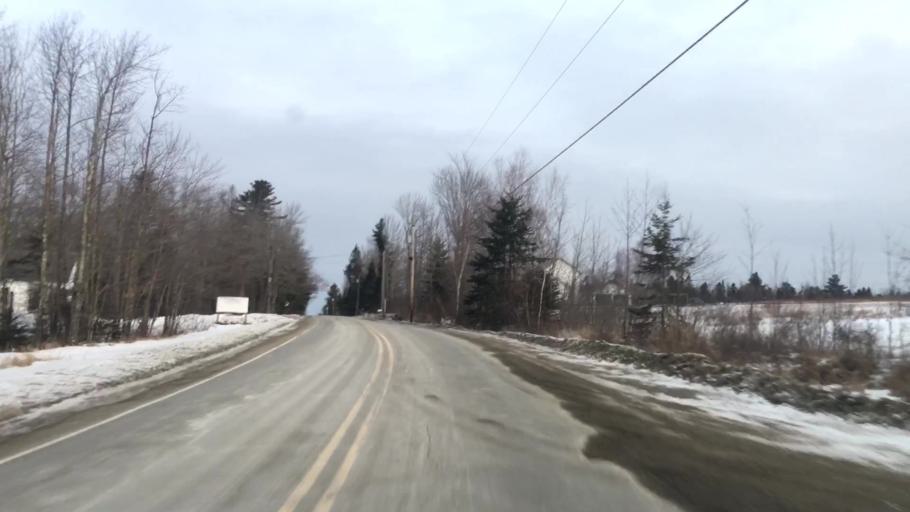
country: US
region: Maine
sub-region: Hancock County
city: Franklin
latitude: 44.7239
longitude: -68.3344
